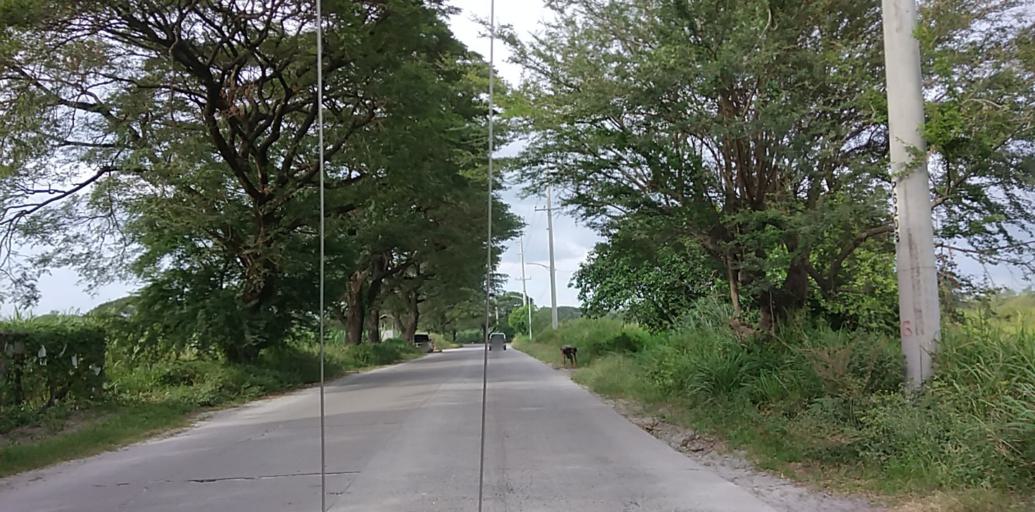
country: PH
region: Central Luzon
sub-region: Province of Pampanga
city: Porac
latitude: 15.0763
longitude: 120.5495
